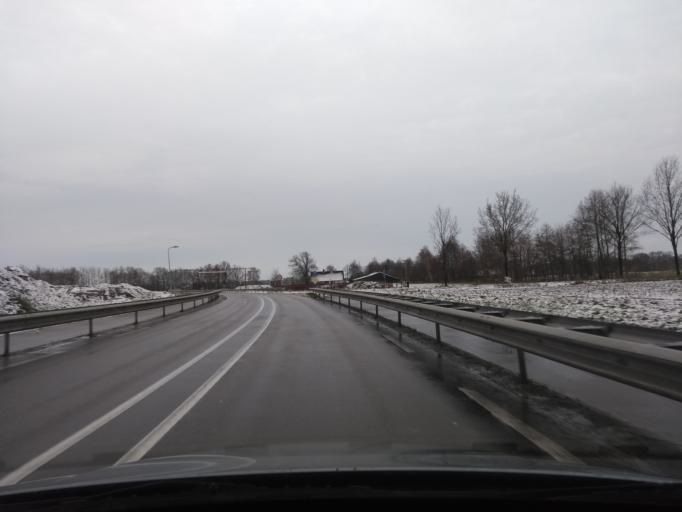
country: NL
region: Overijssel
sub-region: Gemeente Haaksbergen
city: Haaksbergen
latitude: 52.1810
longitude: 6.7380
